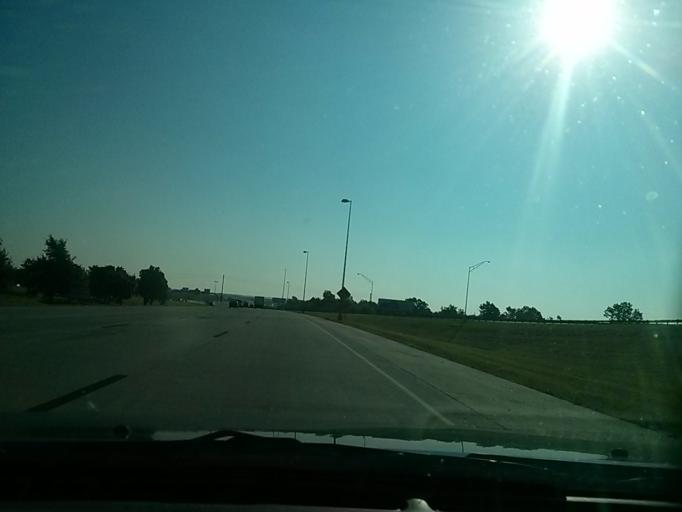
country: US
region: Oklahoma
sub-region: Tulsa County
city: Owasso
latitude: 36.1619
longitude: -95.8810
